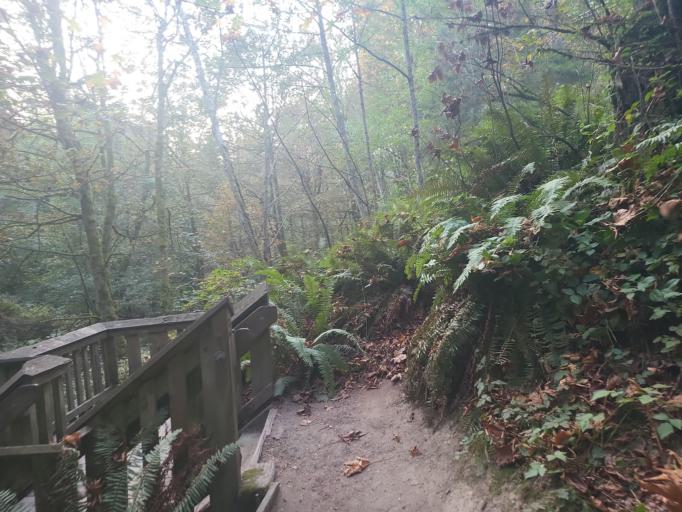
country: US
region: Washington
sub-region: Pierce County
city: Tacoma
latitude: 47.3147
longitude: -122.4117
